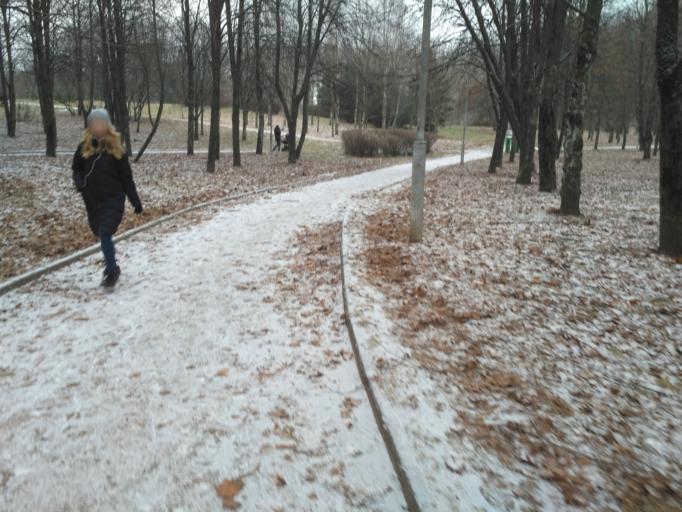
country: BY
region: Minsk
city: Novoye Medvezhino
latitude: 53.9187
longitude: 27.4845
